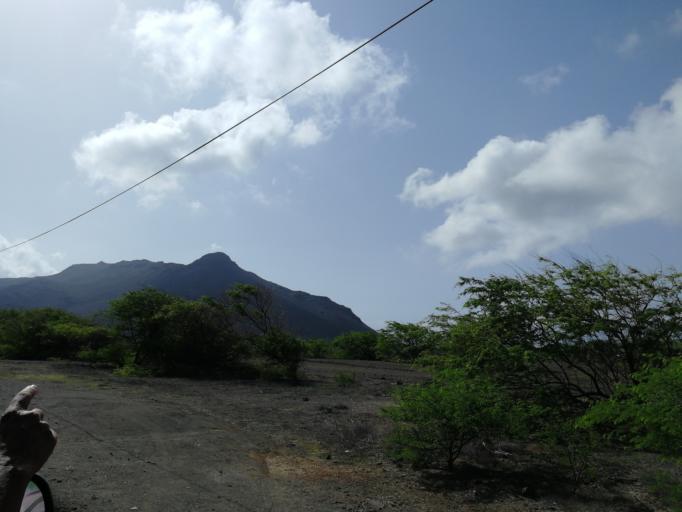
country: CV
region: Sao Vicente
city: Mindelo
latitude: 16.8962
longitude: -24.9294
